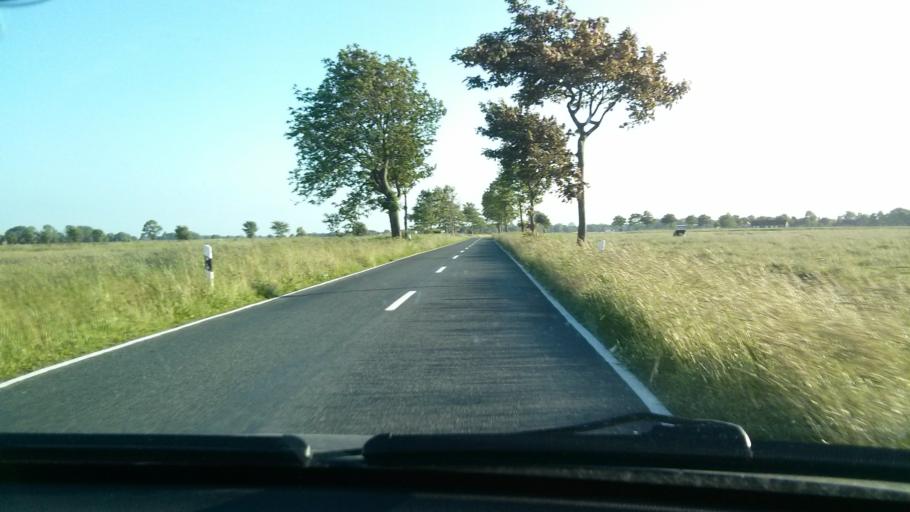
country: DE
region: Lower Saxony
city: Nordenham
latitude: 53.4585
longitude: 8.5188
